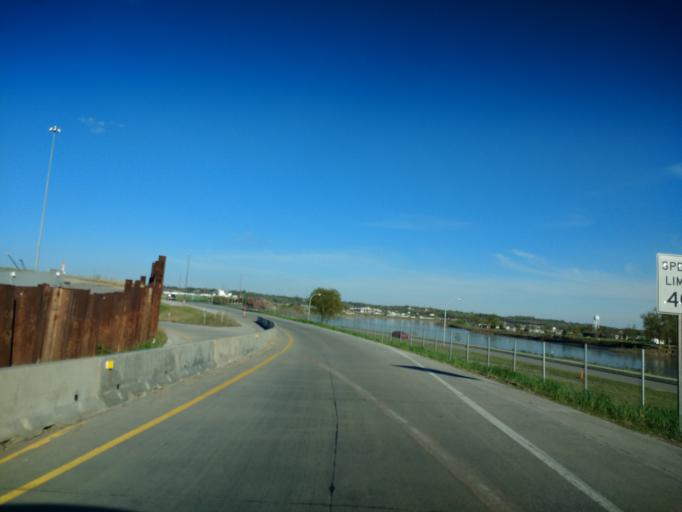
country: US
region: Iowa
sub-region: Woodbury County
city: Sioux City
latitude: 42.4887
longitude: -96.4047
